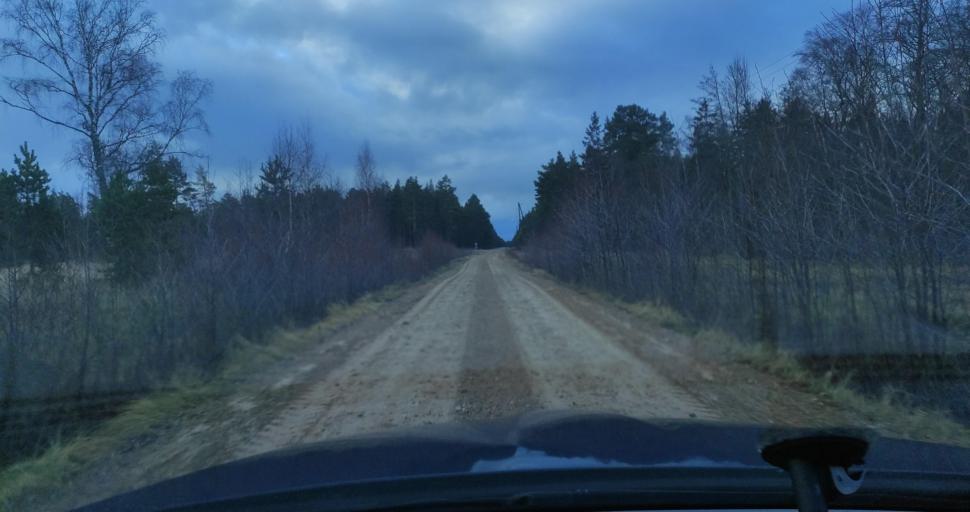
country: LV
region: Pavilostas
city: Pavilosta
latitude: 56.8139
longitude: 21.0650
